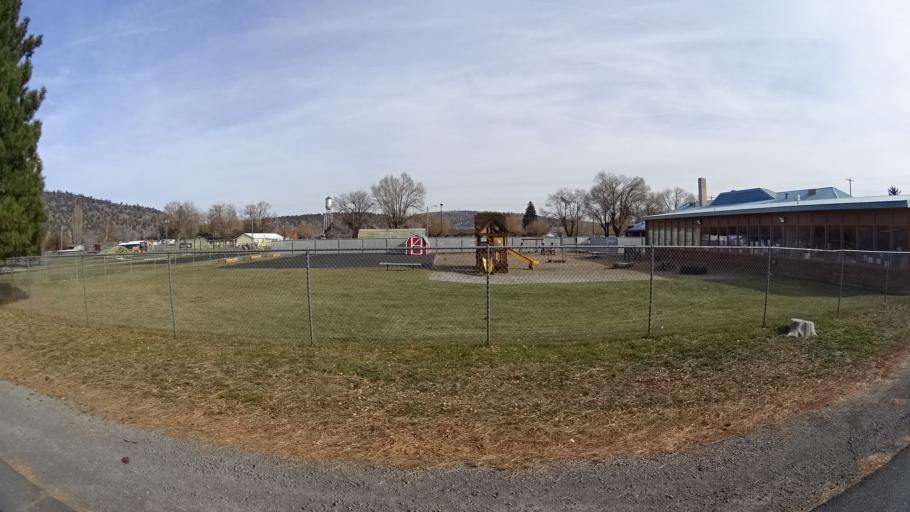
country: US
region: Oregon
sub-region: Klamath County
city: Klamath Falls
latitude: 41.9648
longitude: -121.9254
